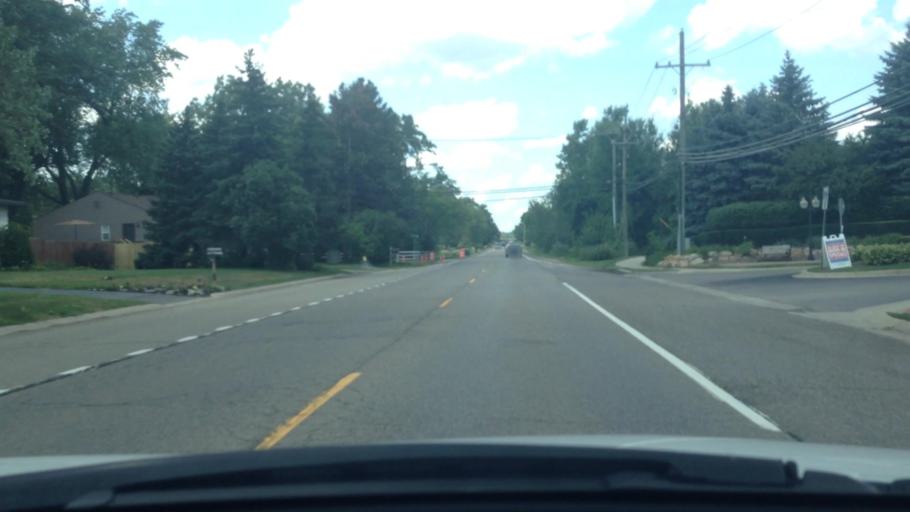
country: US
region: Michigan
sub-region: Oakland County
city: Waterford
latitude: 42.7127
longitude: -83.3490
